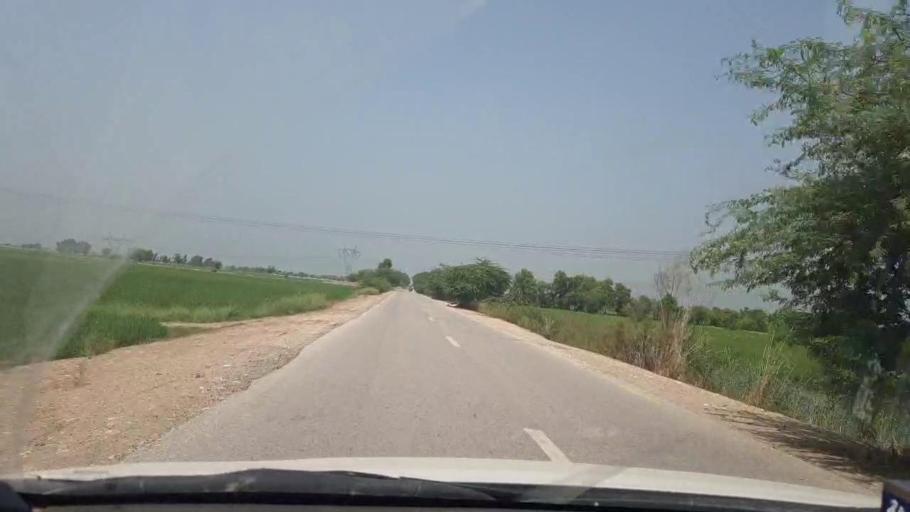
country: PK
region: Sindh
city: Rustam jo Goth
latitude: 27.9563
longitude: 68.7362
